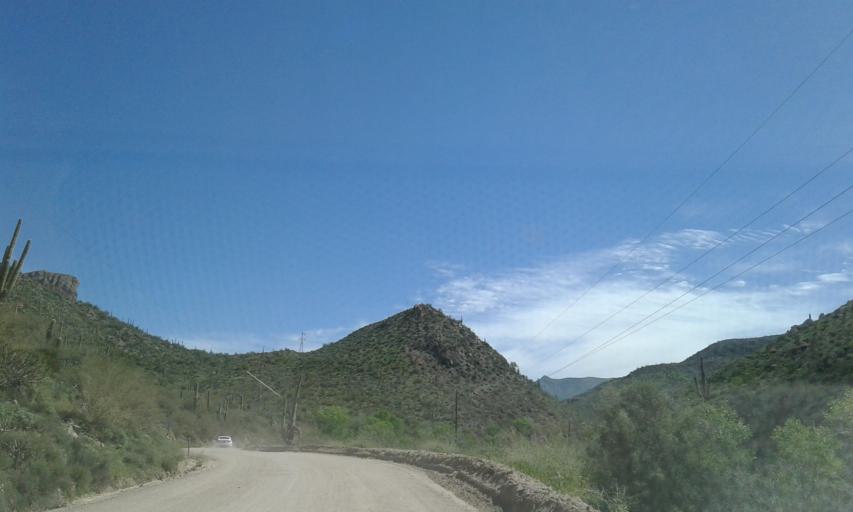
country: US
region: Arizona
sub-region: Pinal County
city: Gold Camp
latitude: 33.5384
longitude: -111.2860
